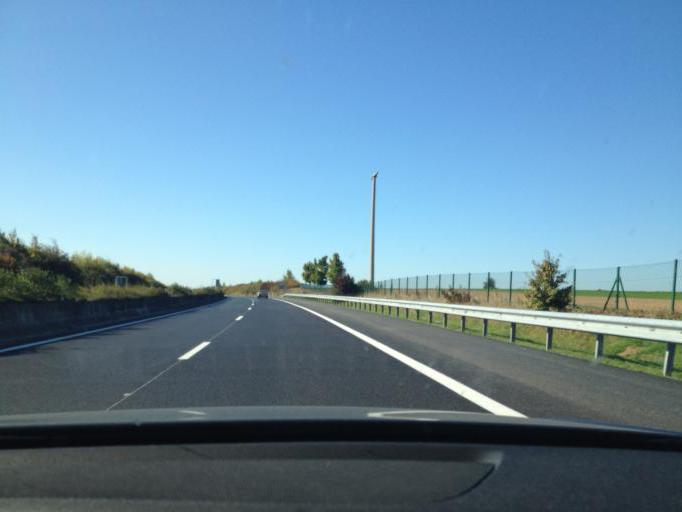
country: LU
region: Grevenmacher
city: Schengen
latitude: 49.4910
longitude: 6.3287
